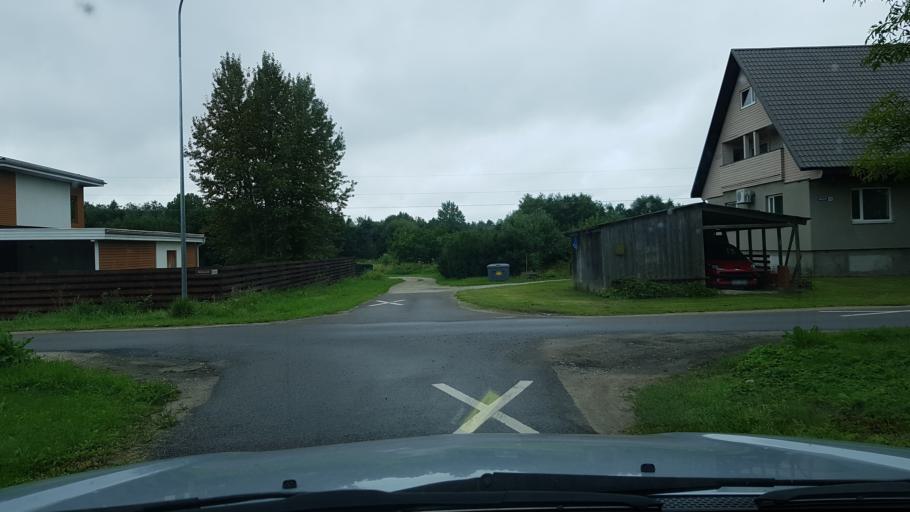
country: EE
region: Harju
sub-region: Rae vald
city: Jueri
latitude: 59.3546
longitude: 24.9220
